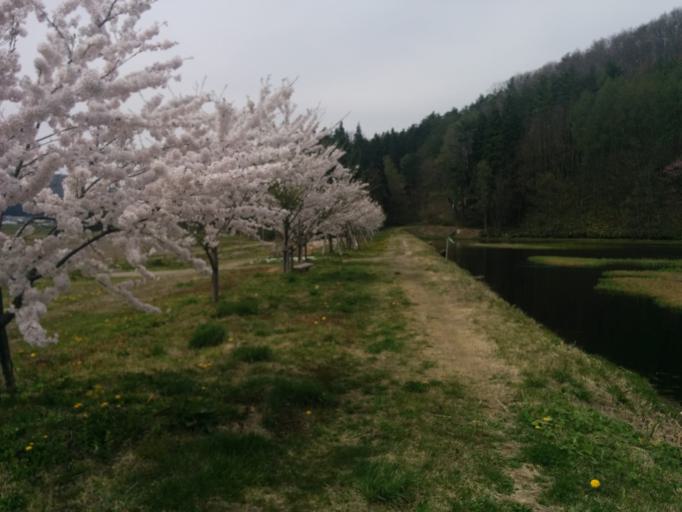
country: JP
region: Fukushima
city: Inawashiro
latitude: 37.4594
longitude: 140.0200
